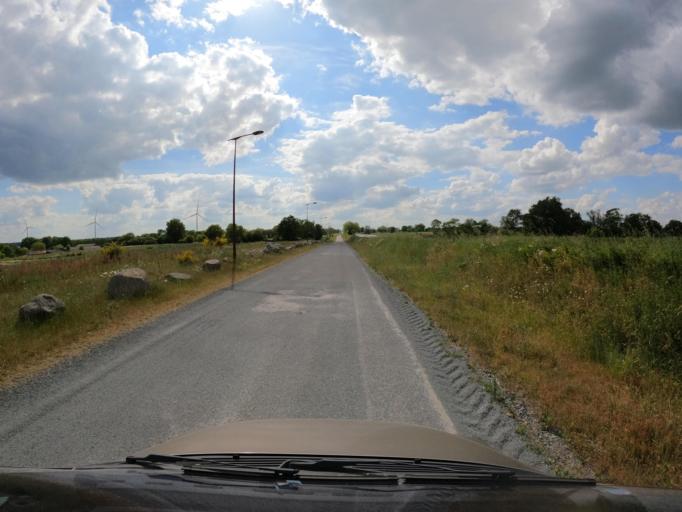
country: FR
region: Pays de la Loire
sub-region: Departement de Maine-et-Loire
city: Coron
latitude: 47.1238
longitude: -0.6720
